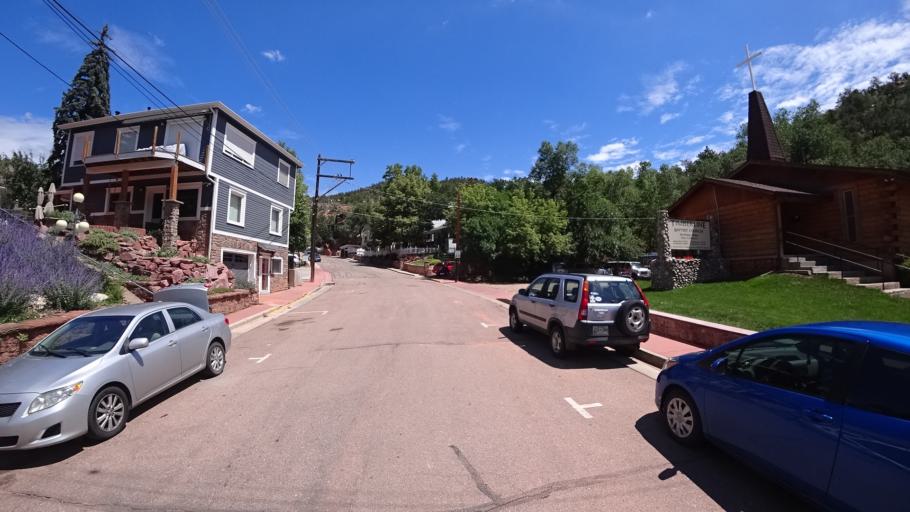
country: US
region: Colorado
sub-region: El Paso County
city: Manitou Springs
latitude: 38.8613
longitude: -104.9169
